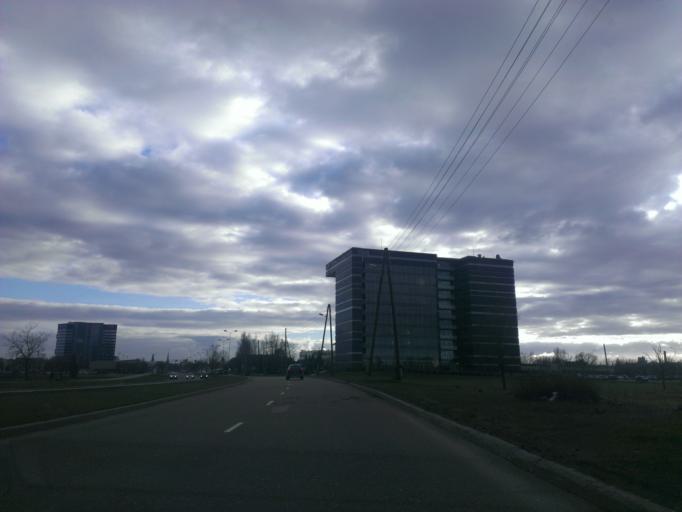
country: LV
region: Riga
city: Riga
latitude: 56.9721
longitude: 24.1215
